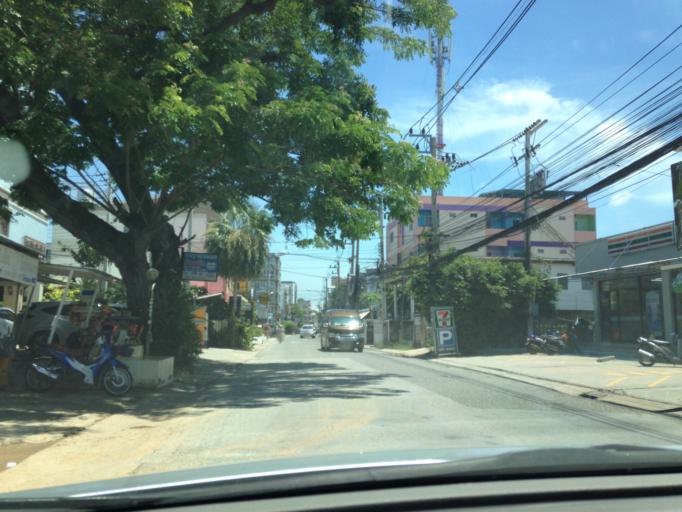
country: TH
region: Chon Buri
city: Chon Buri
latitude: 13.2817
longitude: 100.9193
